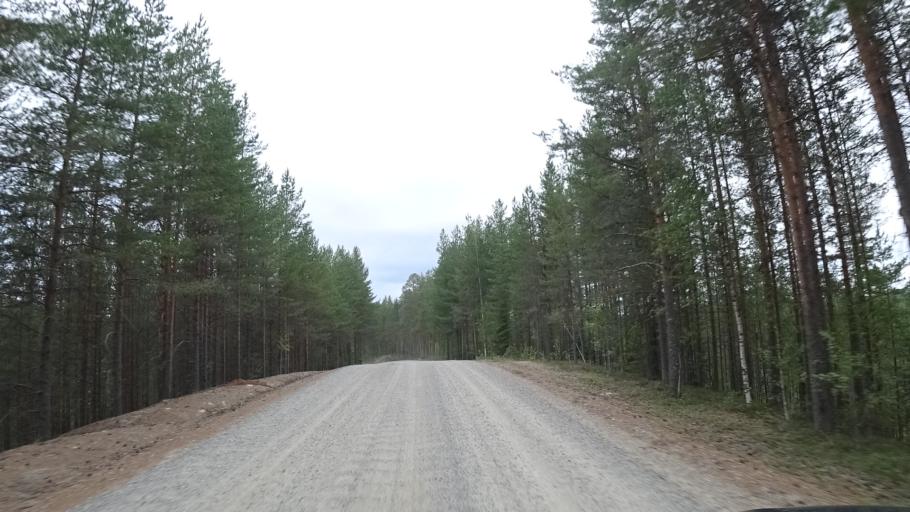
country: FI
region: North Karelia
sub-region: Pielisen Karjala
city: Lieksa
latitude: 63.2354
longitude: 30.3632
